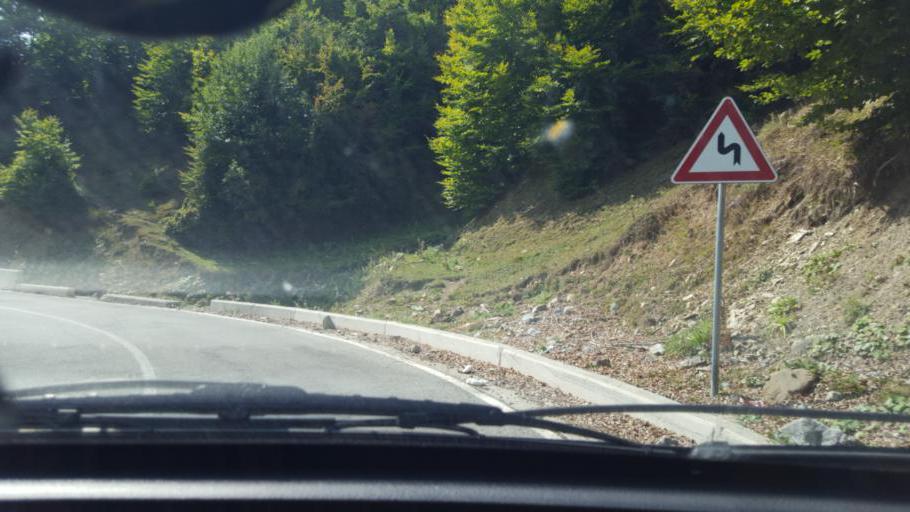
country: AL
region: Kukes
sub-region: Rrethi i Tropojes
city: Valbone
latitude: 42.5453
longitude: 19.7204
